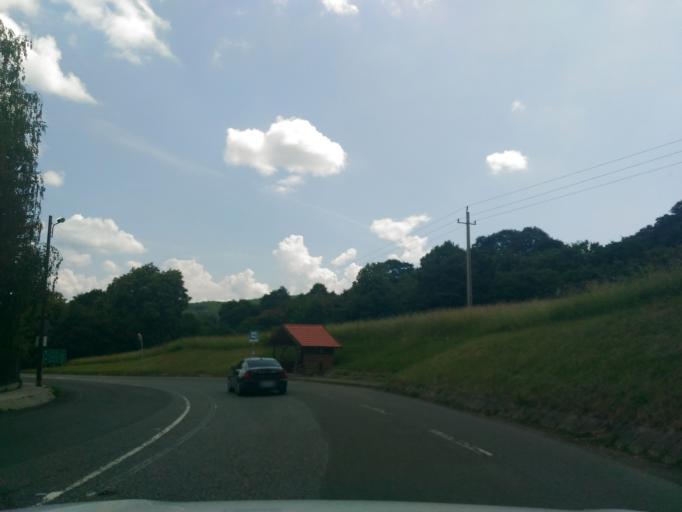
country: HU
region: Baranya
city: Komlo
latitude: 46.1581
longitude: 18.2392
